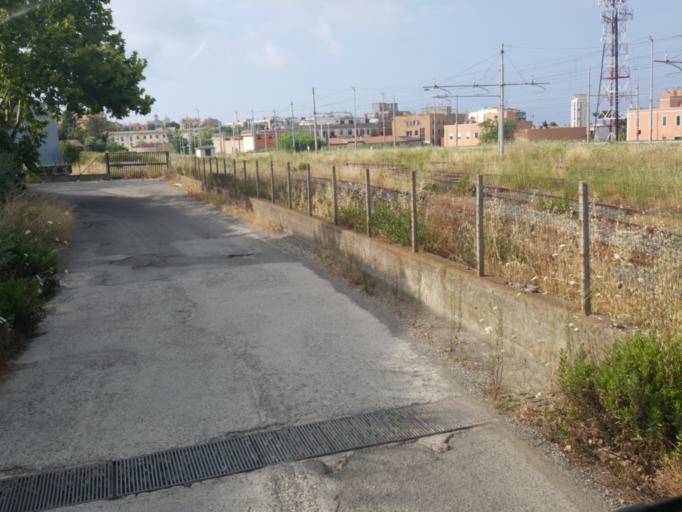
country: IT
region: Latium
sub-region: Citta metropolitana di Roma Capitale
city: Civitavecchia
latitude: 42.0998
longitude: 11.7897
